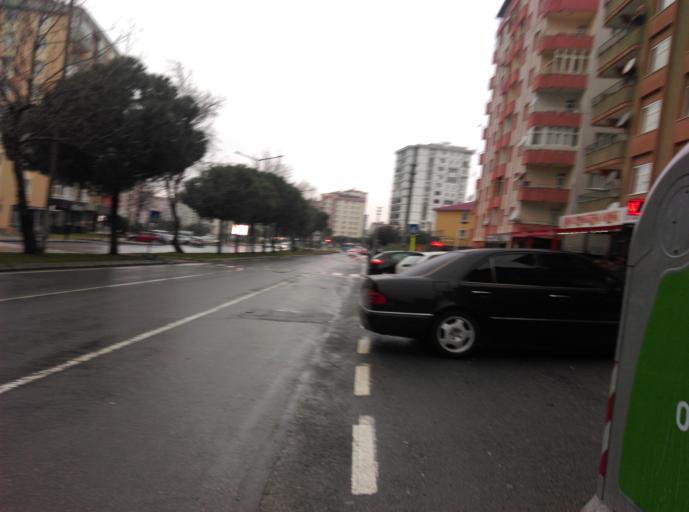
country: TR
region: Kahramanmaras
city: Kahramanmaras
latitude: 37.5842
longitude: 36.8924
